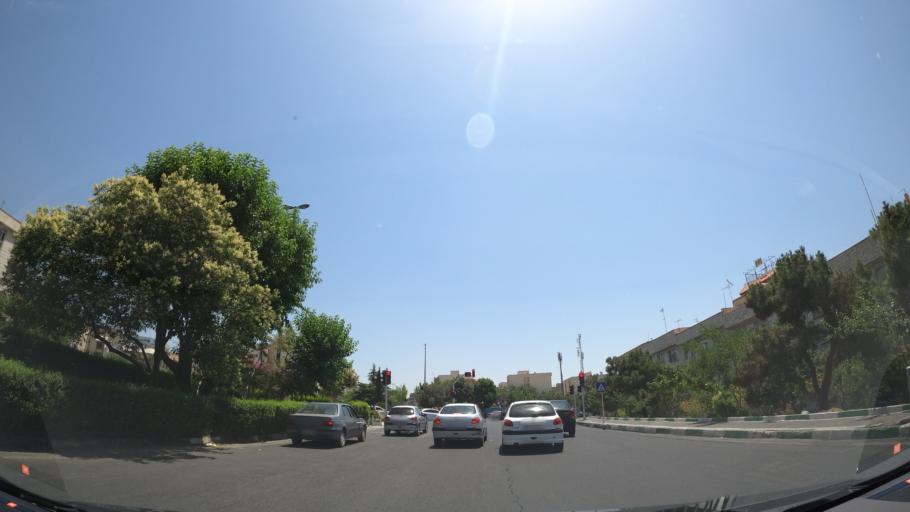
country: IR
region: Tehran
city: Tajrish
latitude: 35.7628
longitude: 51.2890
